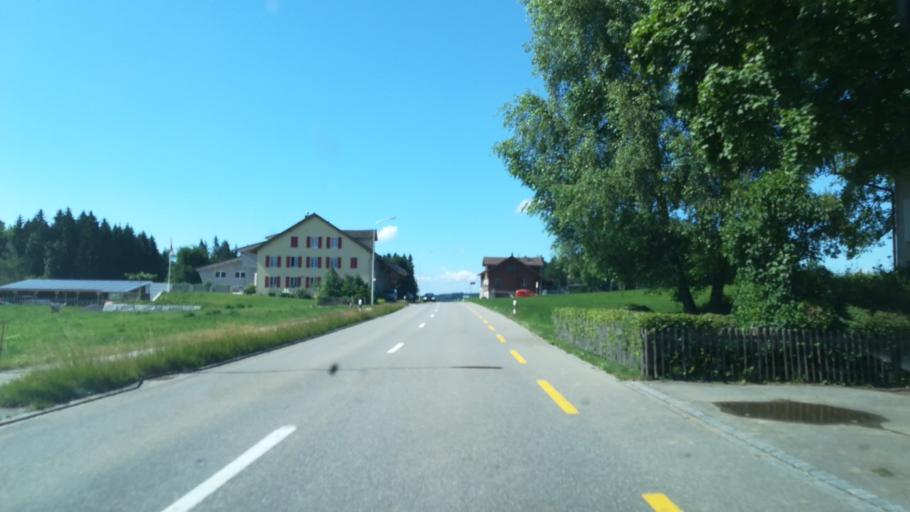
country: CH
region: Saint Gallen
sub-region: Wahlkreis St. Gallen
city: Andwil
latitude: 47.4508
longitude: 9.2546
